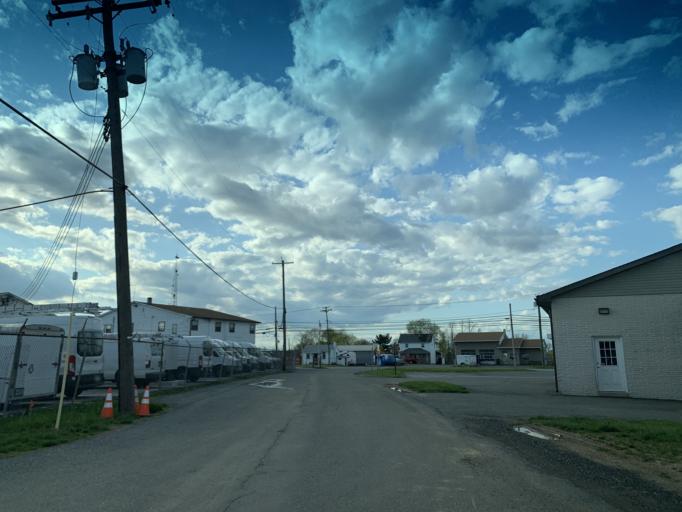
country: US
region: Maryland
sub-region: Harford County
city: Bel Air North
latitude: 39.5783
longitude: -76.3428
